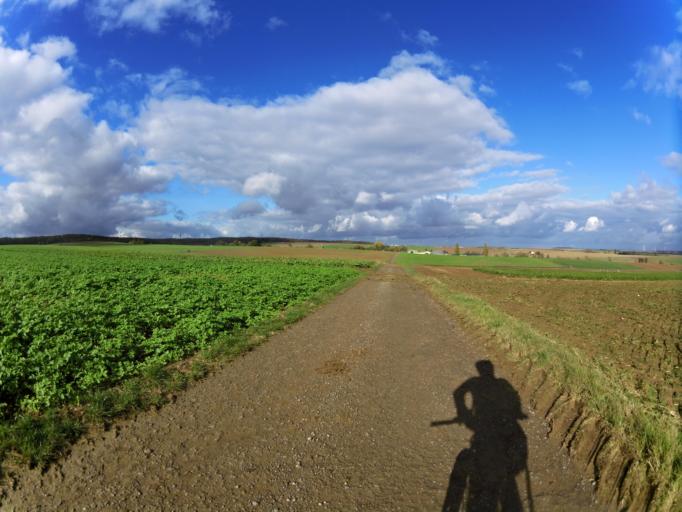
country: DE
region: Bavaria
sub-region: Regierungsbezirk Unterfranken
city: Unterpleichfeld
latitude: 49.8772
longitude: 10.0114
